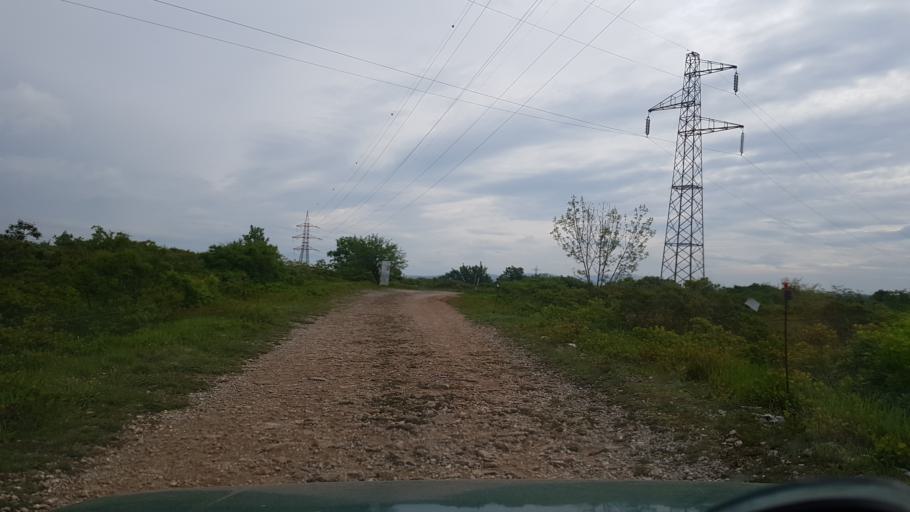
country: IT
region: Friuli Venezia Giulia
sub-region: Provincia di Gorizia
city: Ronchi dei Legionari
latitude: 45.8463
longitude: 13.5076
